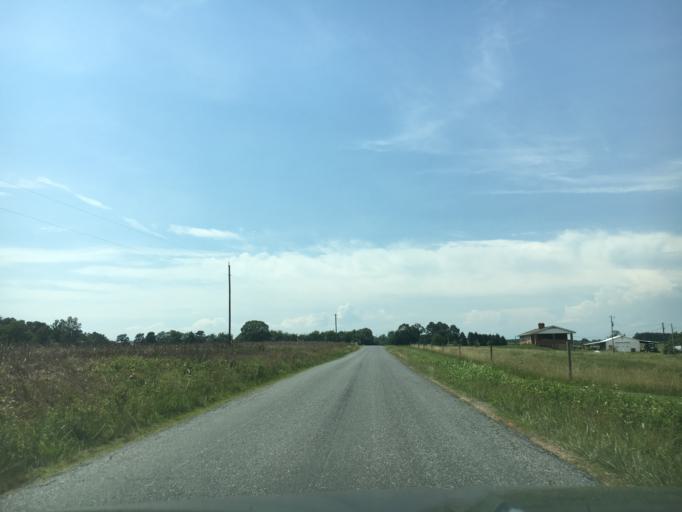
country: US
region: Virginia
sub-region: Pittsylvania County
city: Gretna
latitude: 36.9201
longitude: -79.4253
